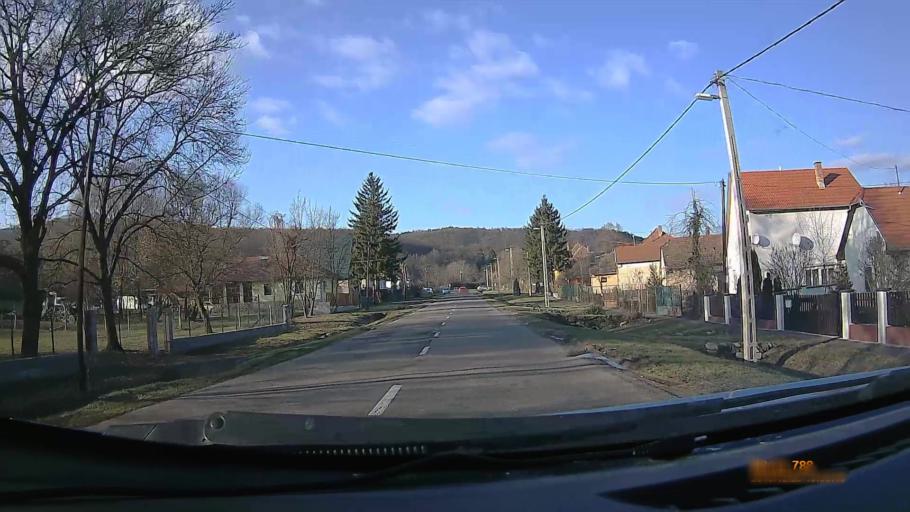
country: HU
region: Heves
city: Sirok
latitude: 47.8977
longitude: 20.1818
